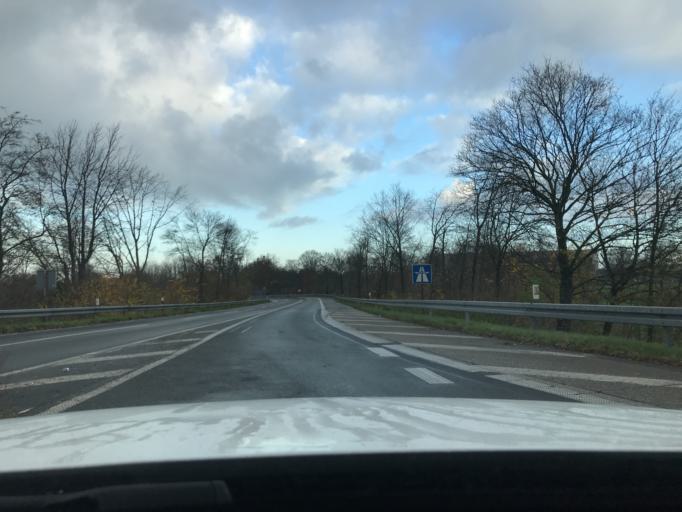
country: DE
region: North Rhine-Westphalia
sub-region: Regierungsbezirk Dusseldorf
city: Krefeld
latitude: 51.3973
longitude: 6.6060
